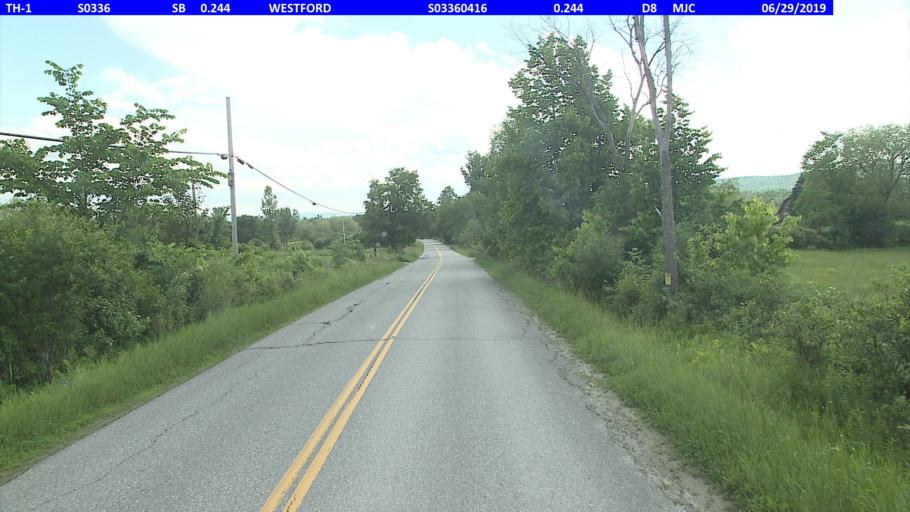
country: US
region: Vermont
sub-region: Chittenden County
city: Milton
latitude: 44.5681
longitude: -73.0606
